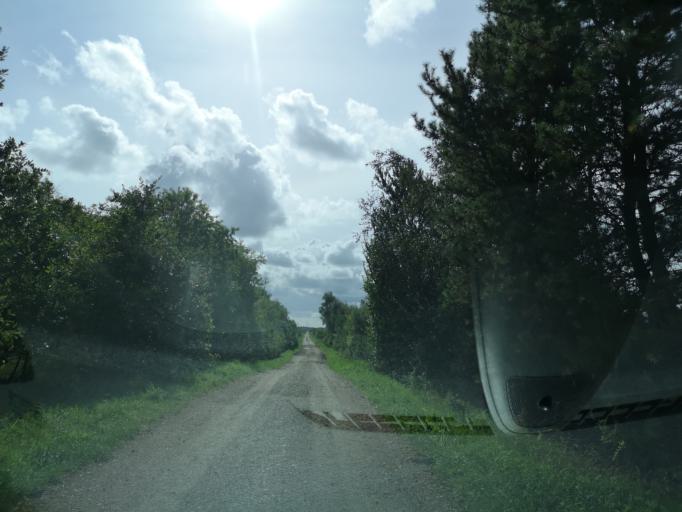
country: DK
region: Central Jutland
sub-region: Ringkobing-Skjern Kommune
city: Tarm
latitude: 55.9412
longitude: 8.5371
